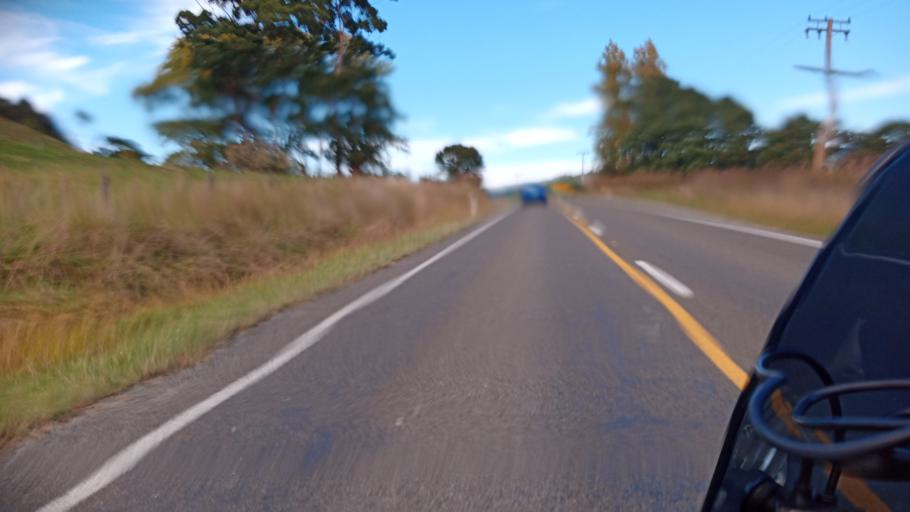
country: NZ
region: Gisborne
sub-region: Gisborne District
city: Gisborne
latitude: -38.7965
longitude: 177.9077
